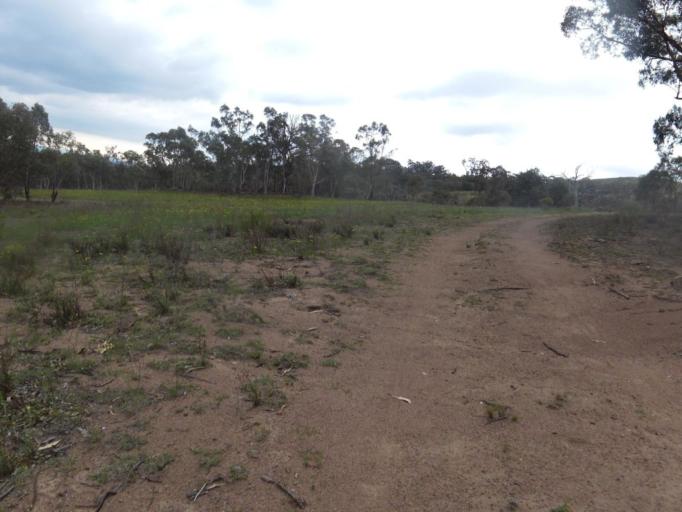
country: AU
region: Australian Capital Territory
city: Forrest
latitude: -35.3501
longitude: 149.1227
